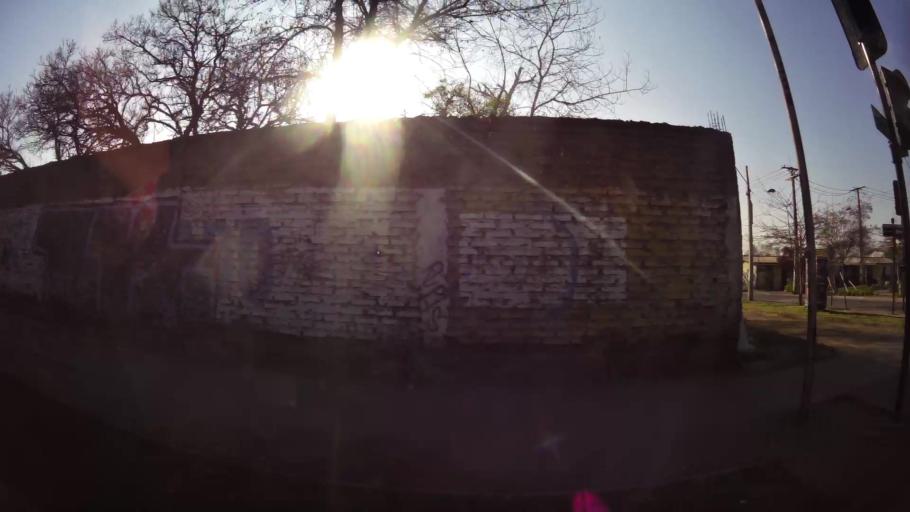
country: CL
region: Santiago Metropolitan
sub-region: Provincia de Santiago
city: Santiago
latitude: -33.4936
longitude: -70.6291
